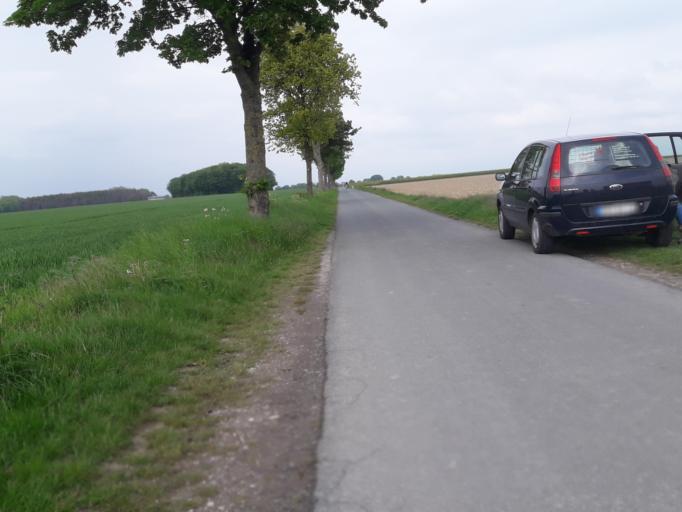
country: DE
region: North Rhine-Westphalia
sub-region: Regierungsbezirk Detmold
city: Paderborn
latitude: 51.6773
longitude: 8.7529
